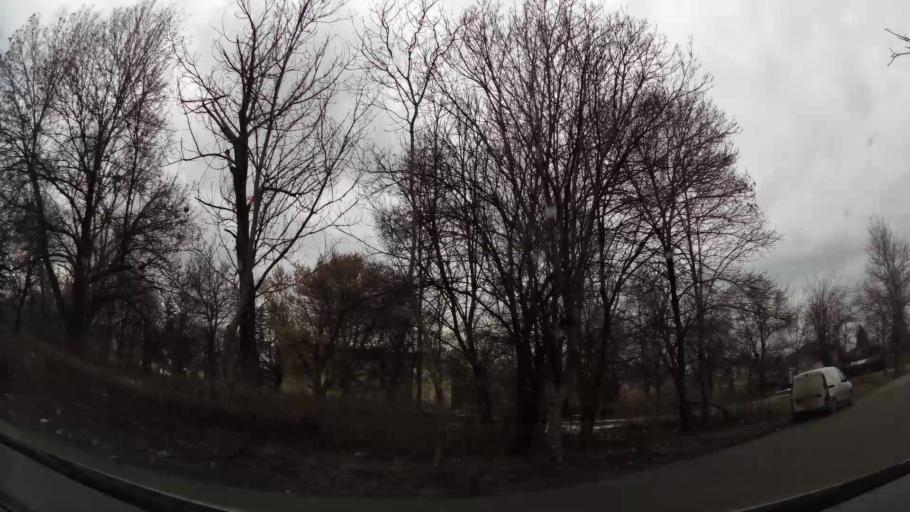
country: BG
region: Sofia-Capital
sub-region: Stolichna Obshtina
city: Sofia
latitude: 42.7224
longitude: 23.2726
